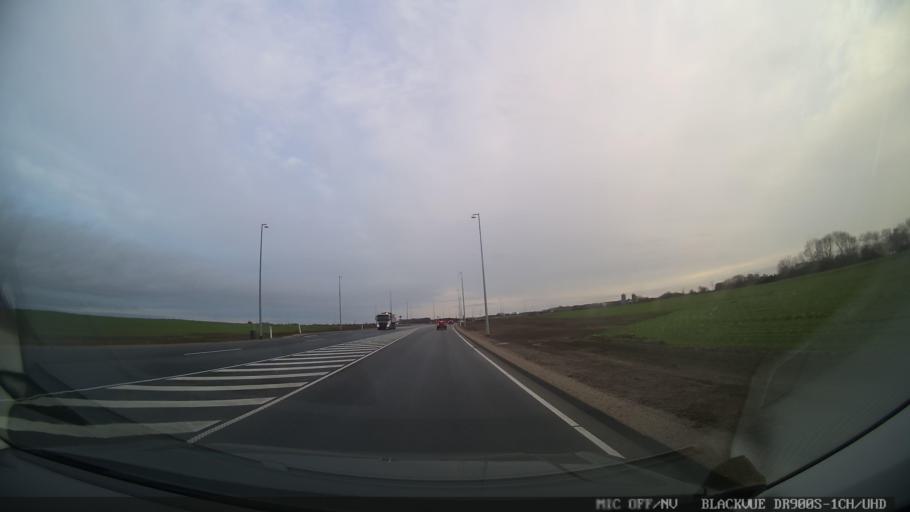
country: DK
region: Central Jutland
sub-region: Arhus Kommune
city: Tranbjerg
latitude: 56.0734
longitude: 10.1344
